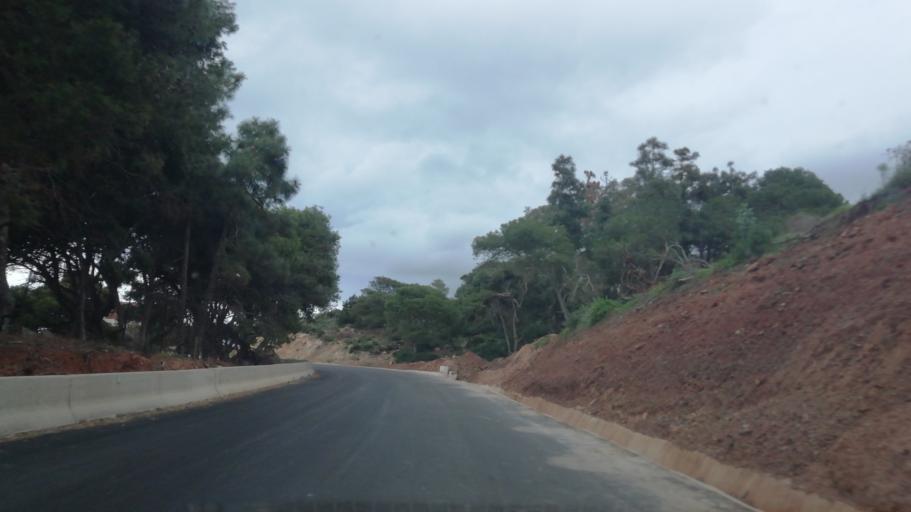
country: DZ
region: Oran
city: Bir el Djir
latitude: 35.7799
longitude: -0.5100
